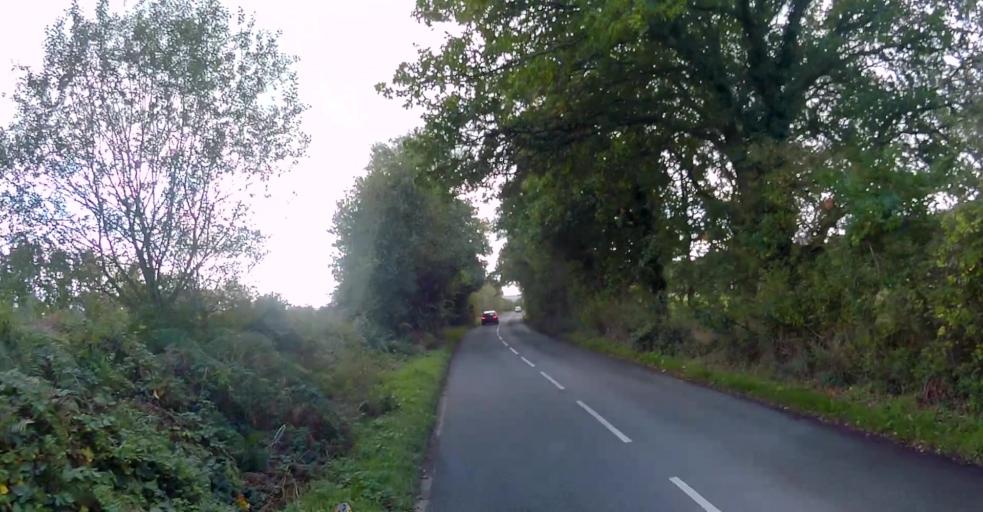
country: GB
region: England
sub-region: Surrey
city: Seale
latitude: 51.1926
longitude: -0.7466
